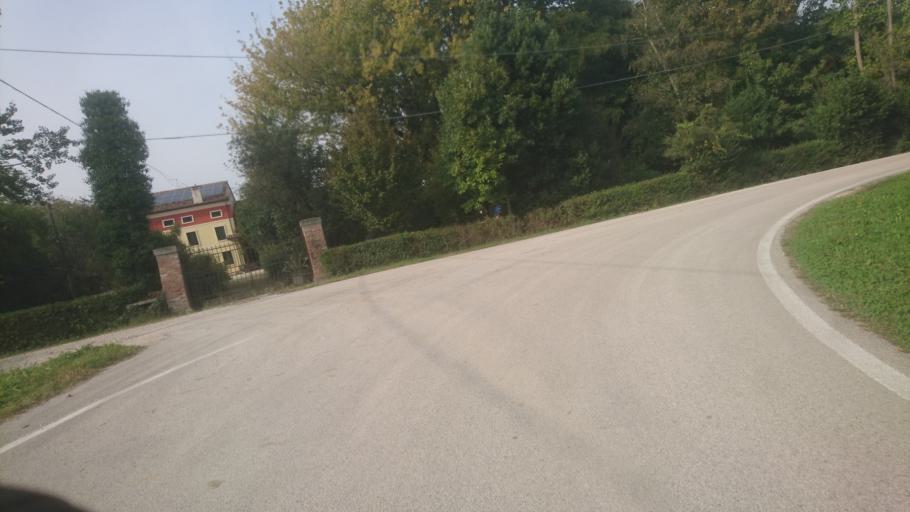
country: IT
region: Veneto
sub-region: Provincia di Vicenza
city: Montegalda
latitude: 45.4673
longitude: 11.6508
